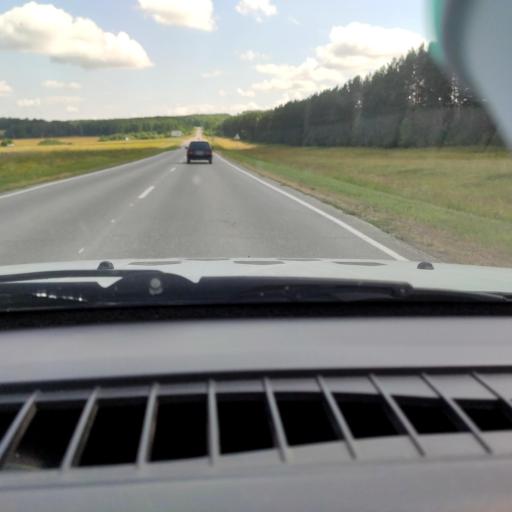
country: RU
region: Bashkortostan
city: Verkhniye Kigi
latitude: 55.3919
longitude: 58.6525
